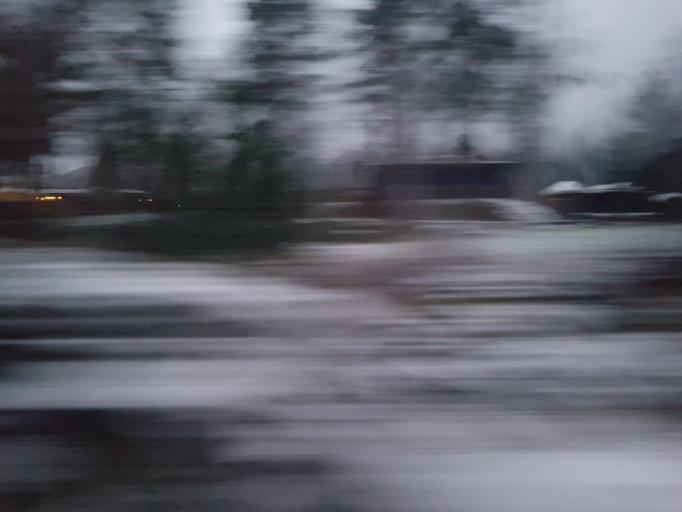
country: NO
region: Oppland
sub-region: Lillehammer
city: Lillehammer
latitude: 61.2297
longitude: 10.4383
